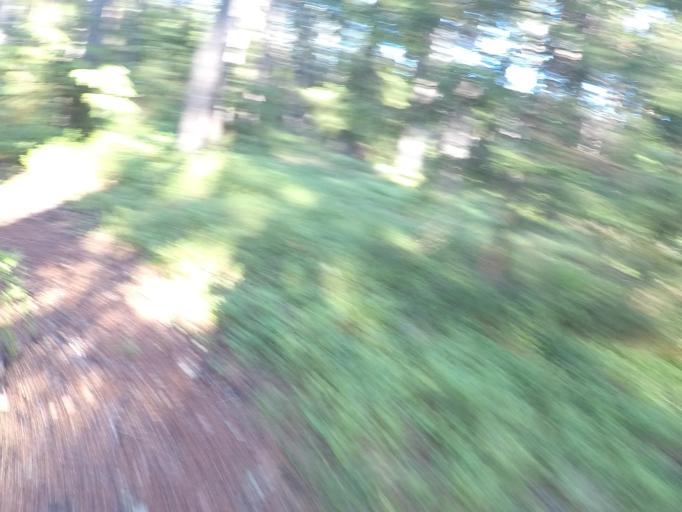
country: SE
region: Soedermanland
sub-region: Eskilstuna Kommun
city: Hallbybrunn
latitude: 59.4005
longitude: 16.3998
